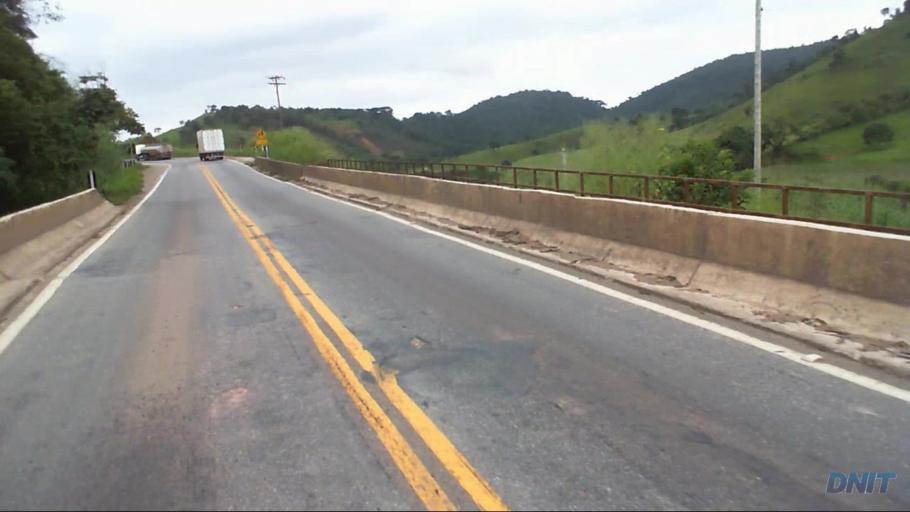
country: BR
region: Minas Gerais
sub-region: Nova Era
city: Nova Era
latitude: -19.7431
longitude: -43.0208
